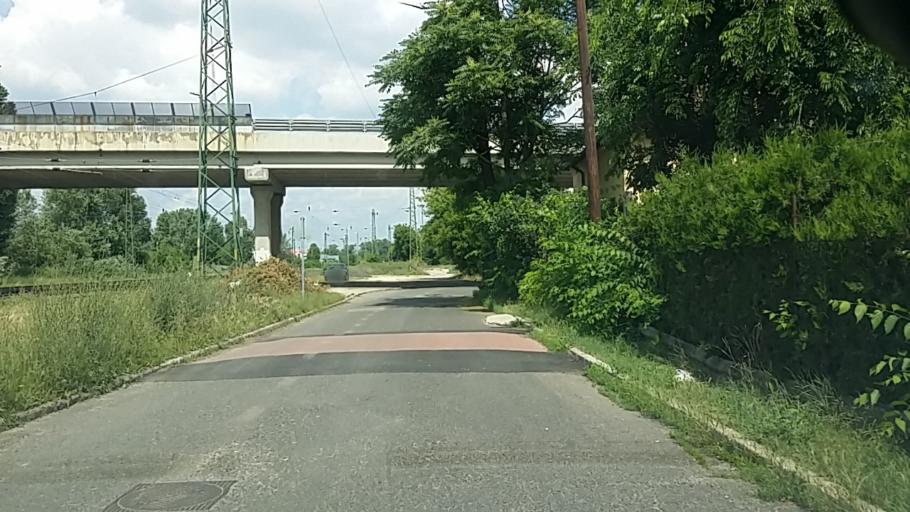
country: HU
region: Budapest
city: Budapest XVI. keruelet
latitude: 47.5192
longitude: 19.1482
